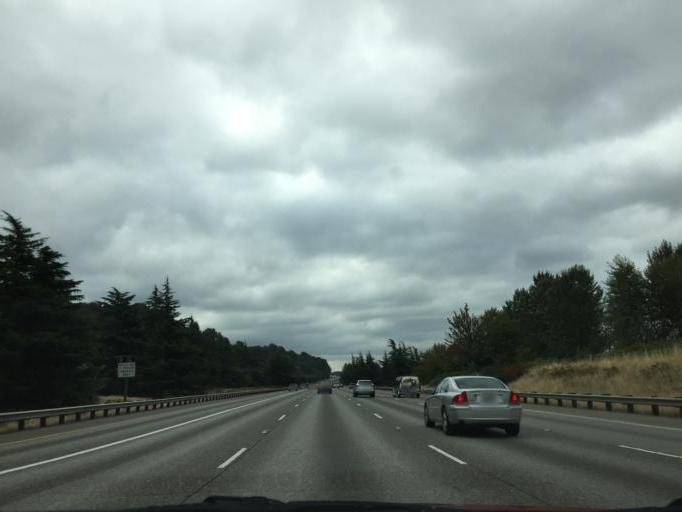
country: US
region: Washington
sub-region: King County
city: Boulevard Park
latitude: 47.5325
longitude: -122.2956
